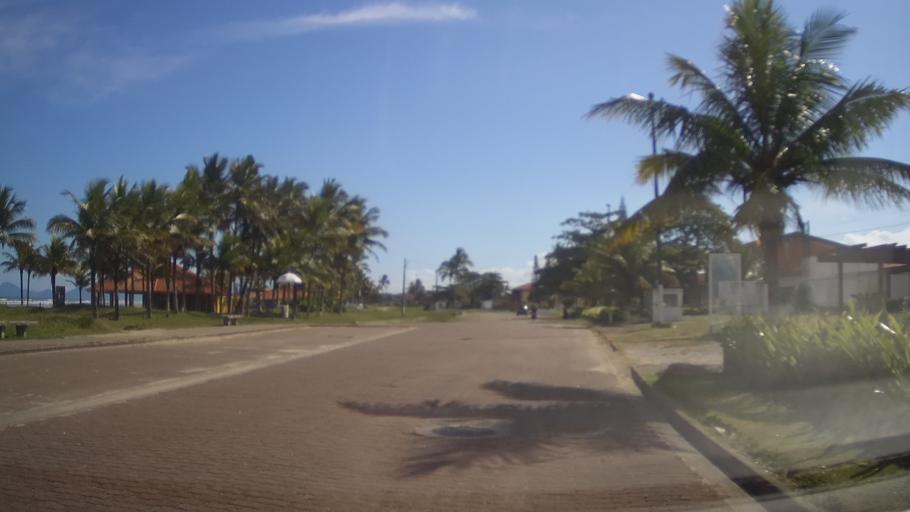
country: BR
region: Sao Paulo
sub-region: Itanhaem
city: Itanhaem
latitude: -24.1998
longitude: -46.8139
